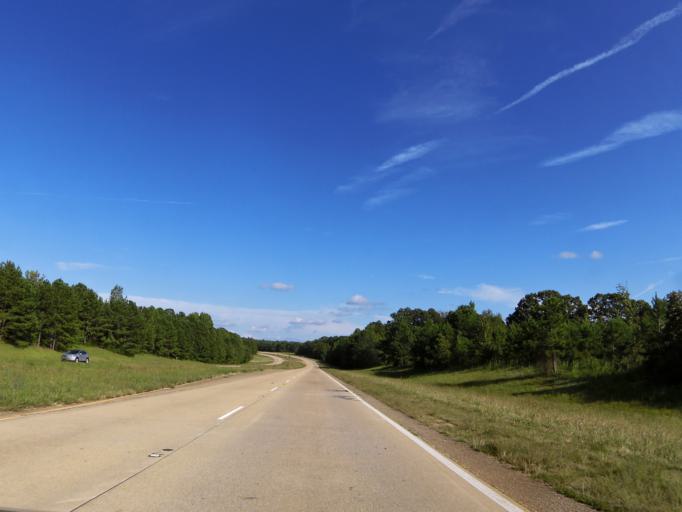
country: US
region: Mississippi
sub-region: Tishomingo County
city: Iuka
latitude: 34.7841
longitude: -88.1831
